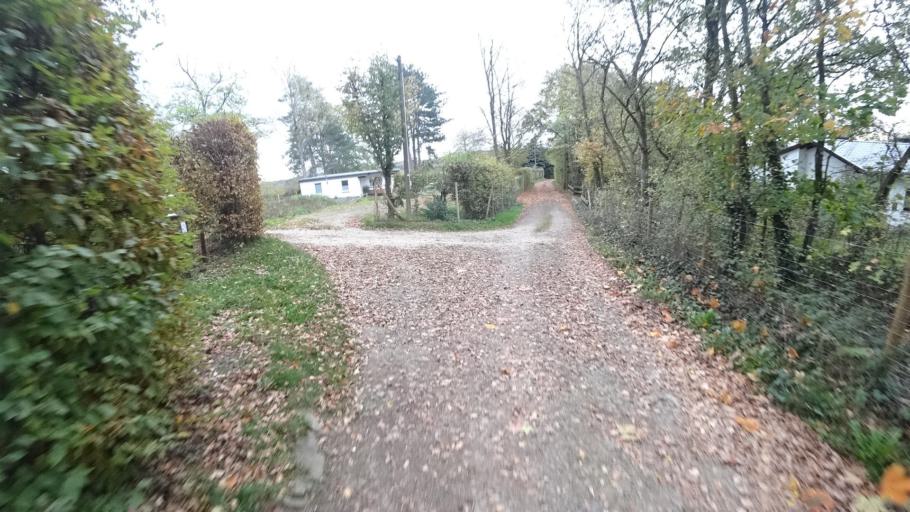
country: DE
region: Rheinland-Pfalz
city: Berg
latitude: 50.5462
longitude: 6.9272
